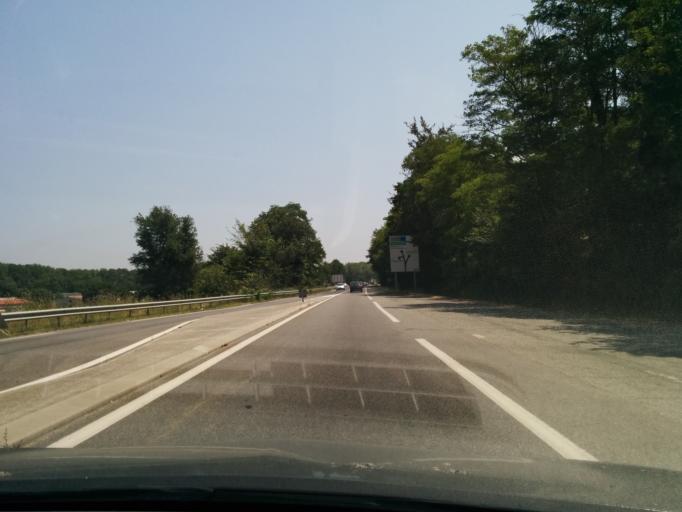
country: FR
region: Midi-Pyrenees
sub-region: Departement de la Haute-Garonne
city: Ayguesvives
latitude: 43.4503
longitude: 1.5911
